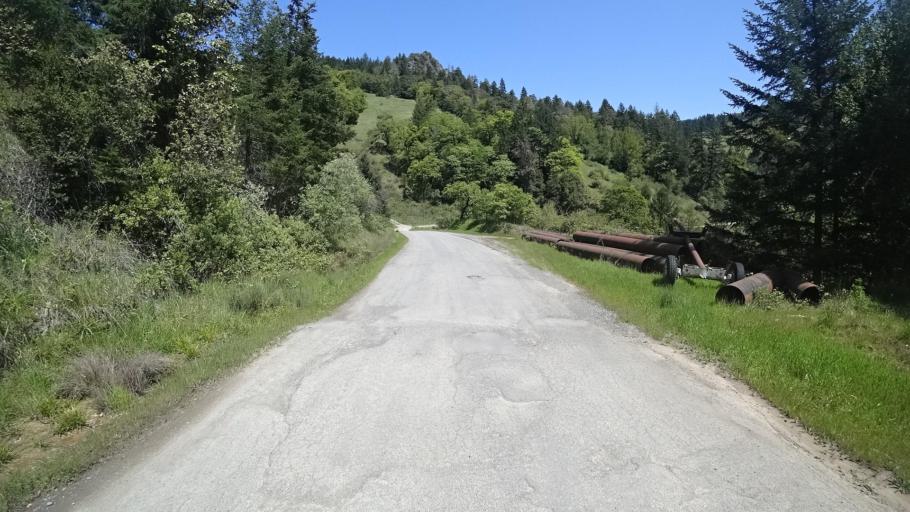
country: US
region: California
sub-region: Humboldt County
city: Redway
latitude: 40.2025
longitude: -123.5244
